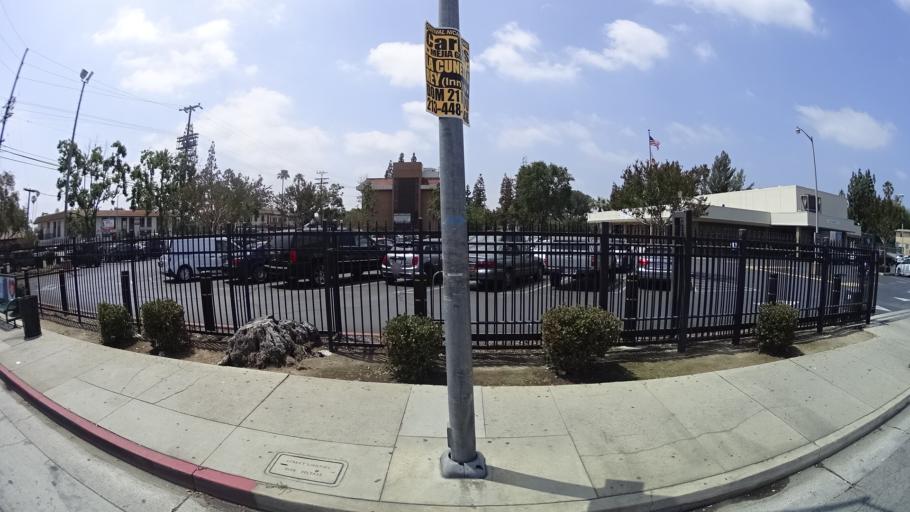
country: US
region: California
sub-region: Los Angeles County
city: Van Nuys
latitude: 34.1938
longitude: -118.4580
